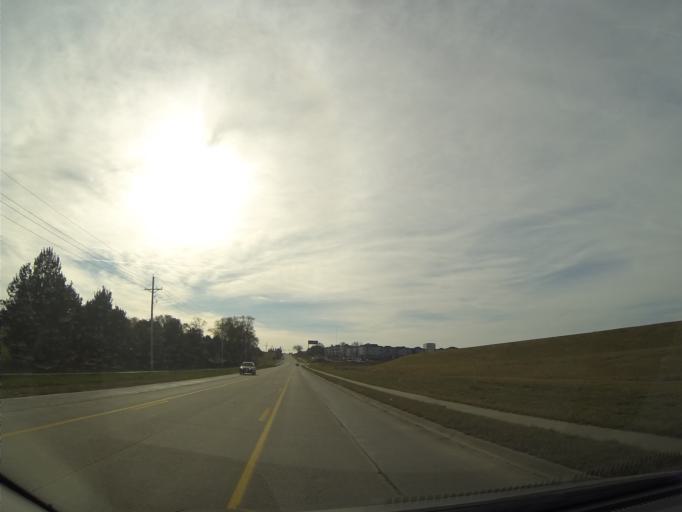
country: US
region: Nebraska
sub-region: Douglas County
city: Elkhorn
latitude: 41.2728
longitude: -96.2157
